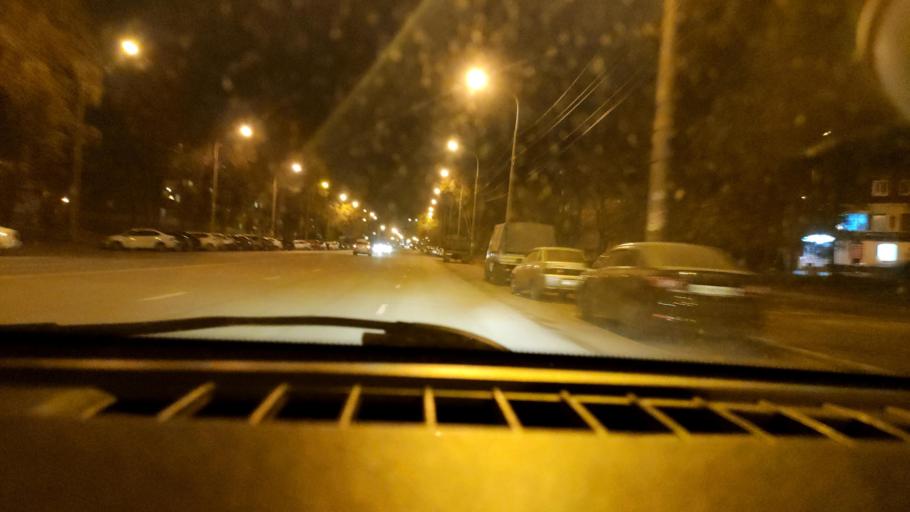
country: RU
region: Samara
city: Samara
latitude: 53.2262
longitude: 50.2105
